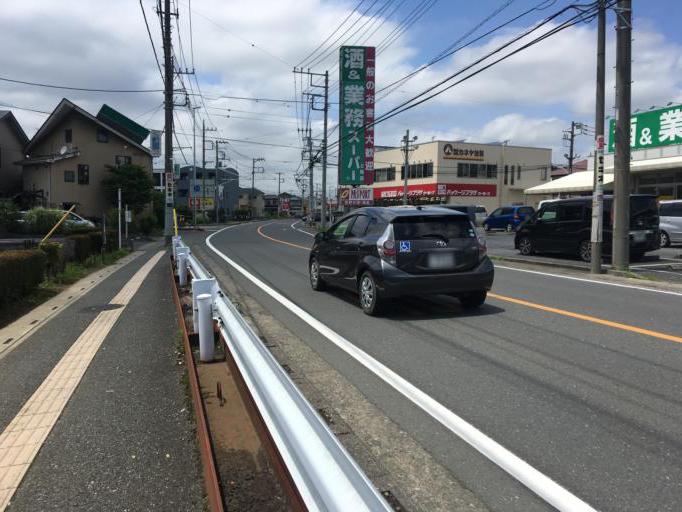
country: JP
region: Saitama
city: Okegawa
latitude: 35.9889
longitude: 139.5765
